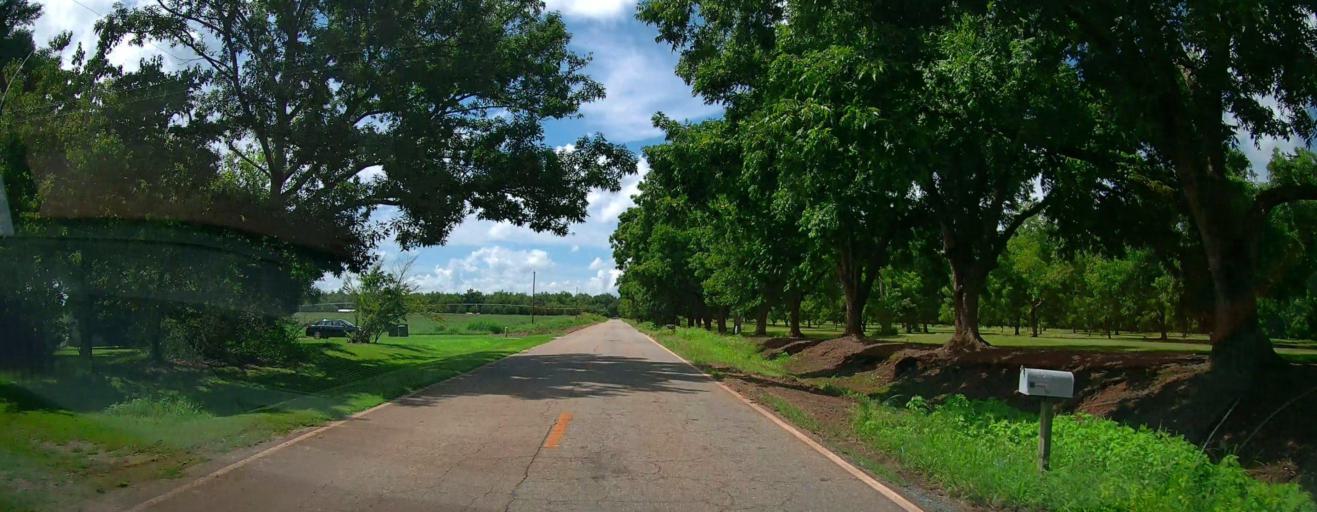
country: US
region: Georgia
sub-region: Houston County
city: Perry
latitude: 32.5210
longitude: -83.7805
